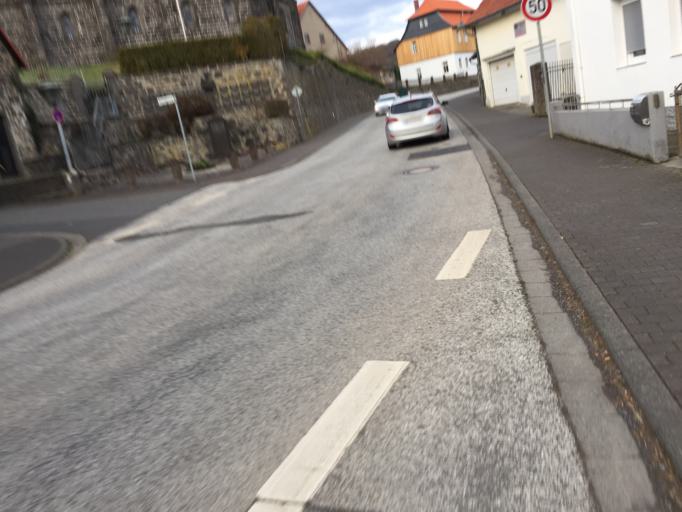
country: DE
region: Hesse
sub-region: Regierungsbezirk Giessen
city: Rabenau
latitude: 50.6744
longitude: 8.8619
